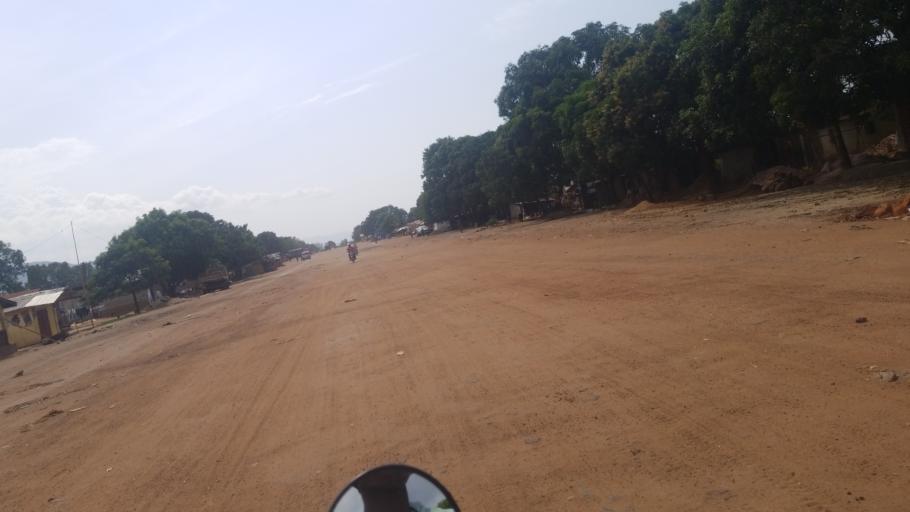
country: SL
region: Western Area
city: Waterloo
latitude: 8.3385
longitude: -13.0452
